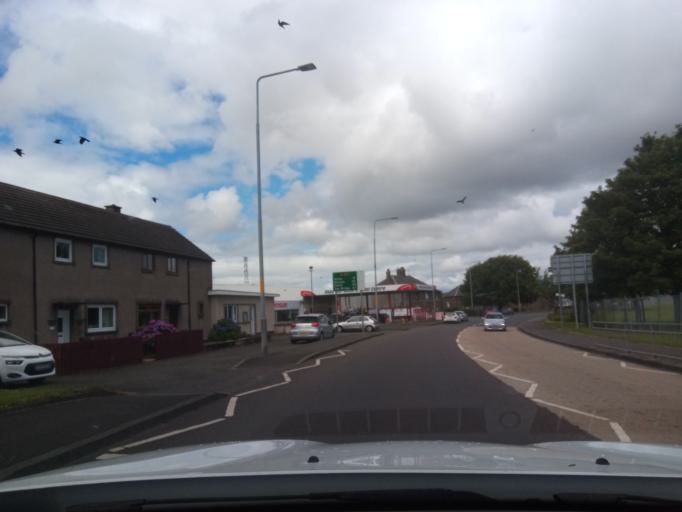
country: GB
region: Scotland
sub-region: Fife
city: Kincardine
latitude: 56.0694
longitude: -3.7180
